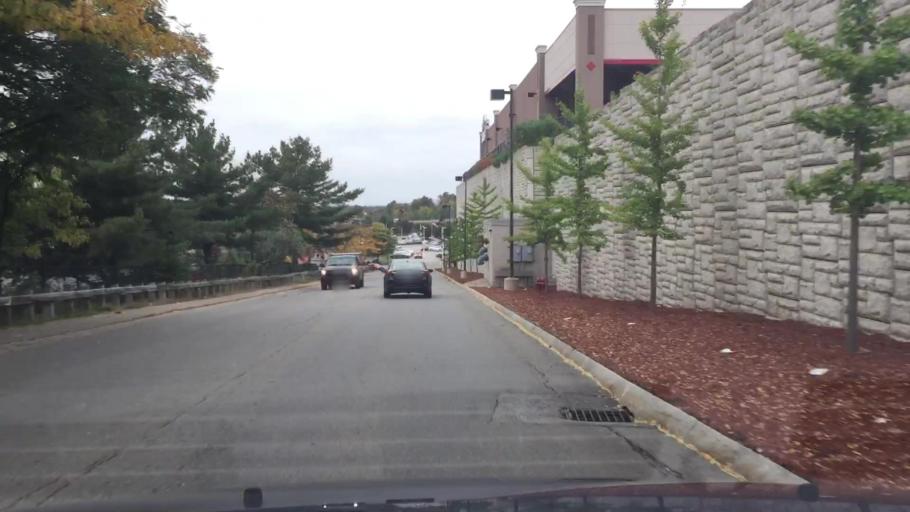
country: US
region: New Hampshire
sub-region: Hillsborough County
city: Hudson
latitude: 42.7272
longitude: -71.4482
